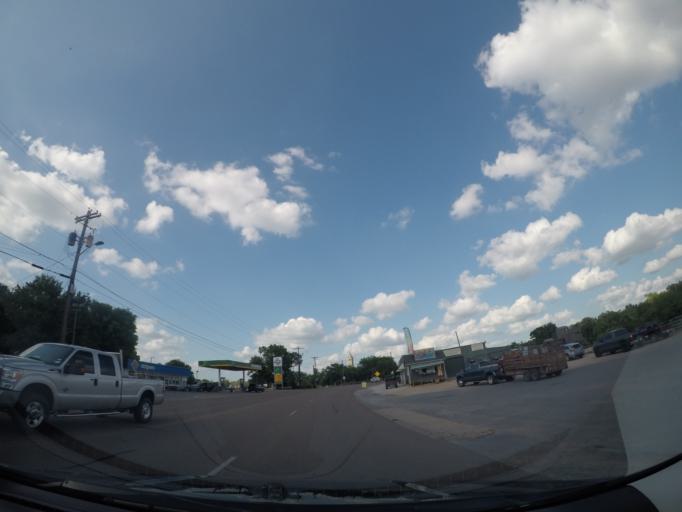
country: US
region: Texas
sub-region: Lavaca County
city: Hallettsville
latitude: 29.4429
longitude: -96.9466
